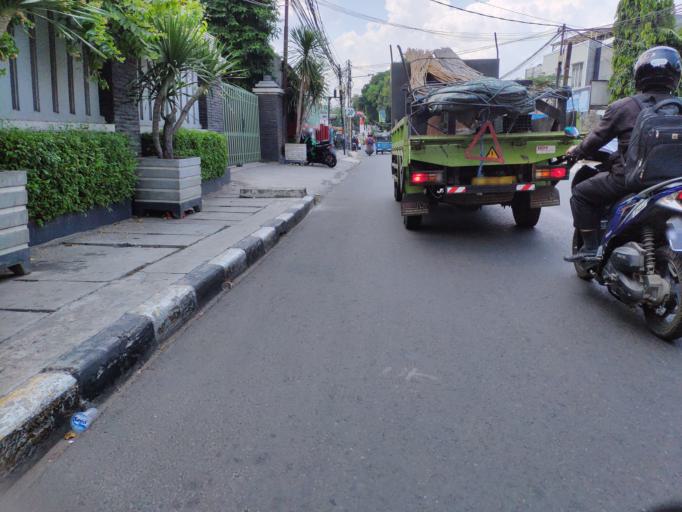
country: ID
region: Jakarta Raya
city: Jakarta
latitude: -6.1966
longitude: 106.8724
